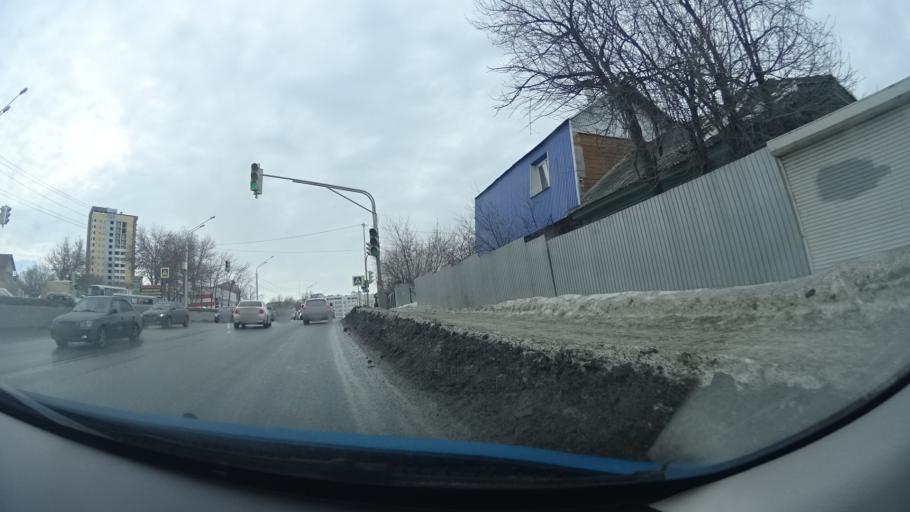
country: RU
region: Bashkortostan
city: Ufa
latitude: 54.7020
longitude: 55.9784
